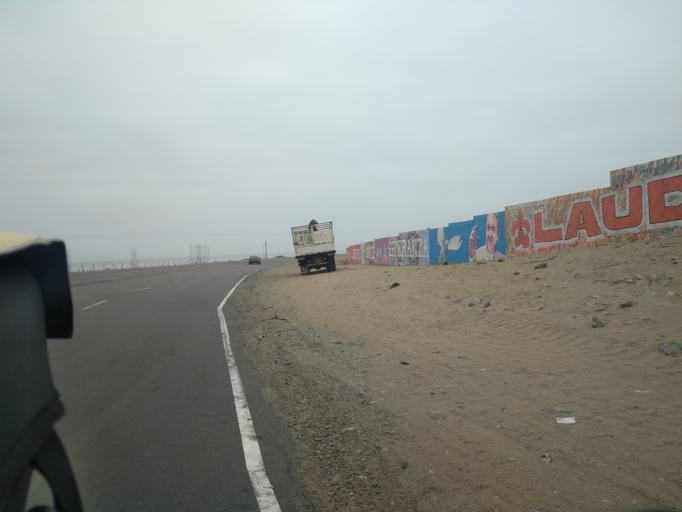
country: PE
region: La Libertad
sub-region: Provincia de Trujillo
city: Huanchaco
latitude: -8.0974
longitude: -79.1111
